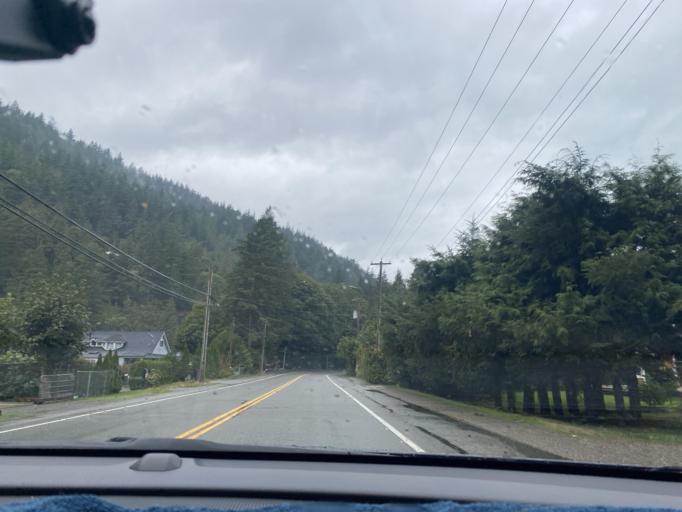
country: CA
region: British Columbia
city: Agassiz
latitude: 49.2942
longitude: -121.7824
